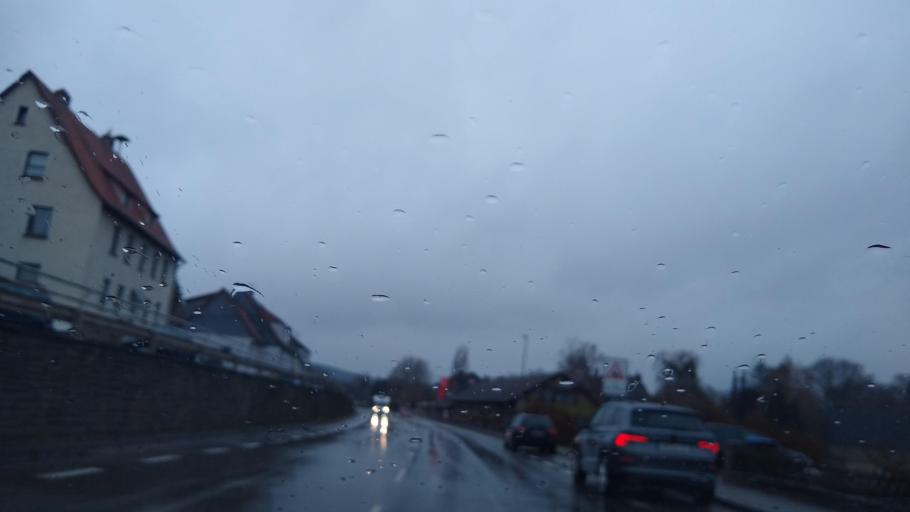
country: DE
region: Lower Saxony
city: Hehlen
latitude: 51.9852
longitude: 9.4767
